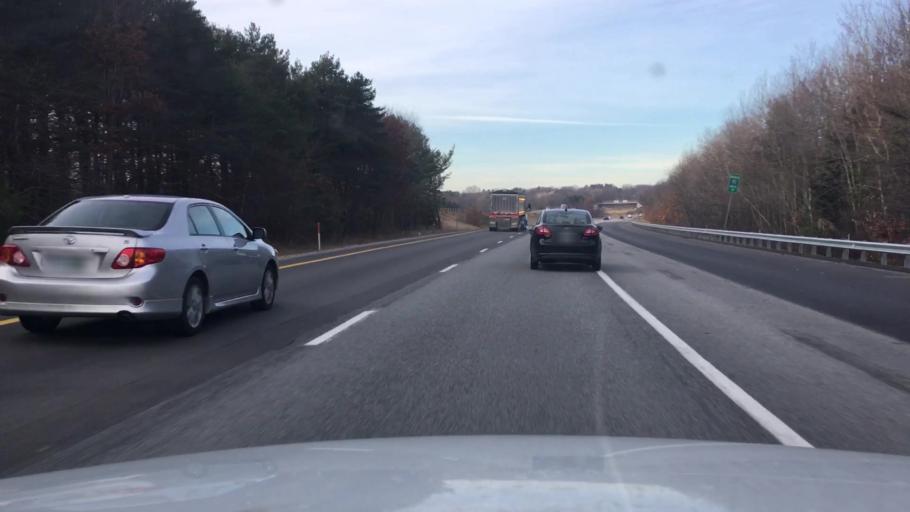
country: US
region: New Hampshire
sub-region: Hillsborough County
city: Manchester
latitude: 42.9613
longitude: -71.4090
